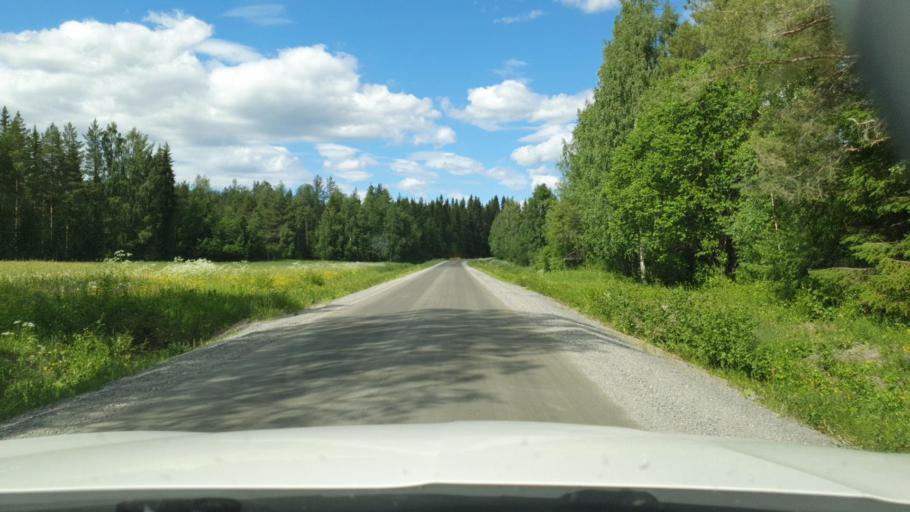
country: SE
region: Vaesterbotten
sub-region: Skelleftea Kommun
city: Forsbacka
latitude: 64.8128
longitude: 20.4946
